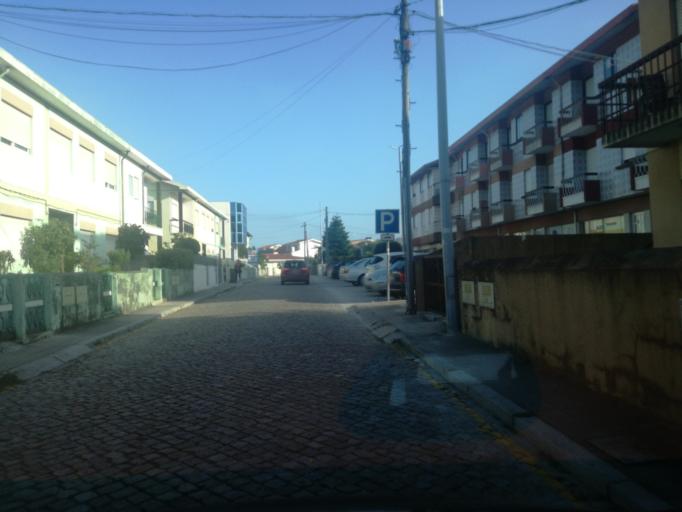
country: PT
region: Porto
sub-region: Maia
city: Gemunde
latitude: 41.2490
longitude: -8.6589
